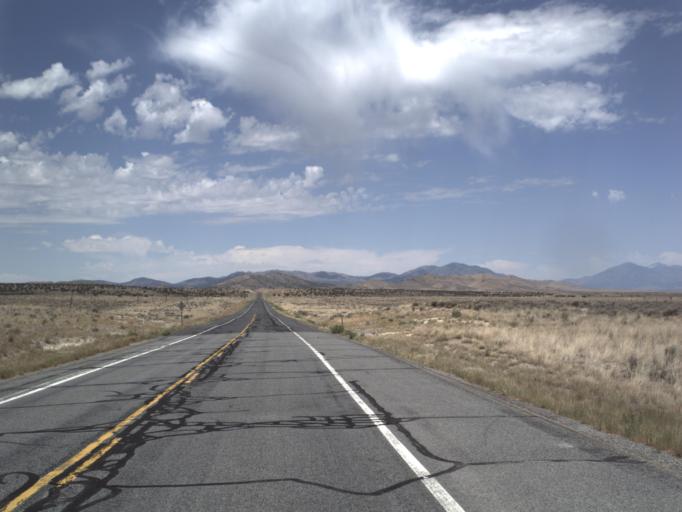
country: US
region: Utah
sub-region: Utah County
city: Eagle Mountain
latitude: 40.0535
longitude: -112.2993
